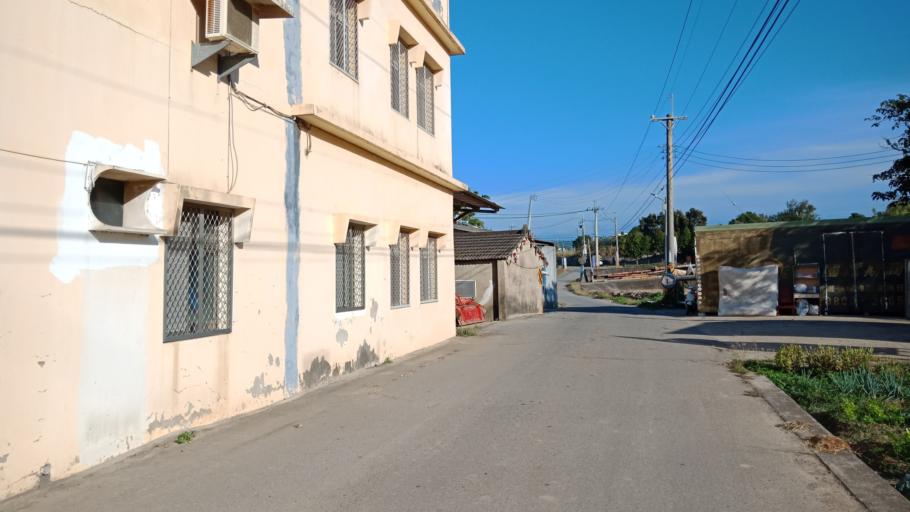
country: TW
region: Taiwan
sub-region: Miaoli
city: Miaoli
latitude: 24.4844
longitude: 120.7024
